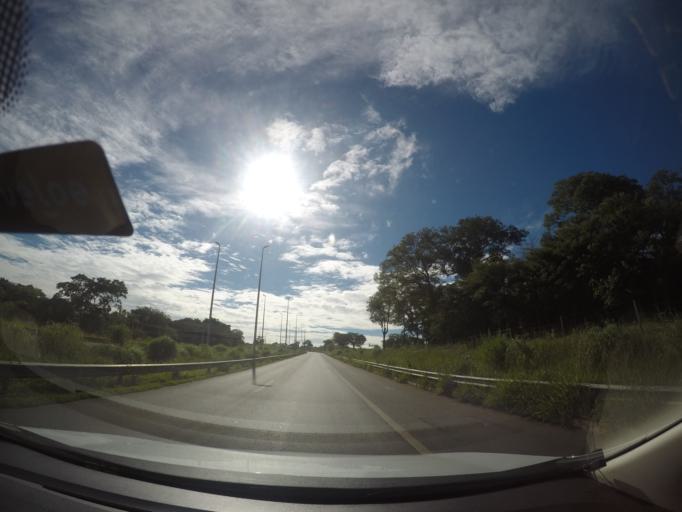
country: BR
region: Goias
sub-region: Goiania
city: Goiania
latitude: -16.6901
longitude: -49.1742
